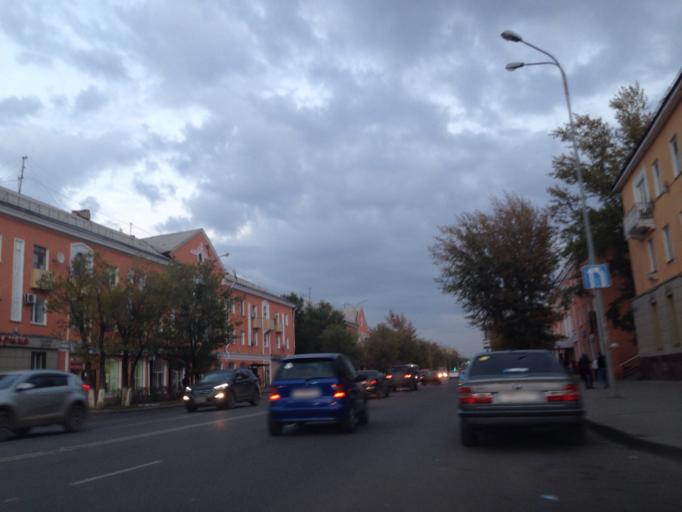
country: KZ
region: Astana Qalasy
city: Astana
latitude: 51.1911
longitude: 71.4075
